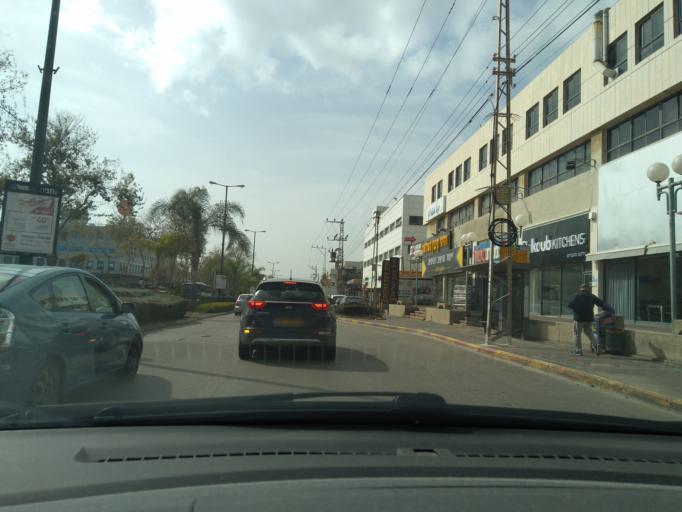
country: IL
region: Central District
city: Even Yehuda
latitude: 32.2801
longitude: 34.8609
